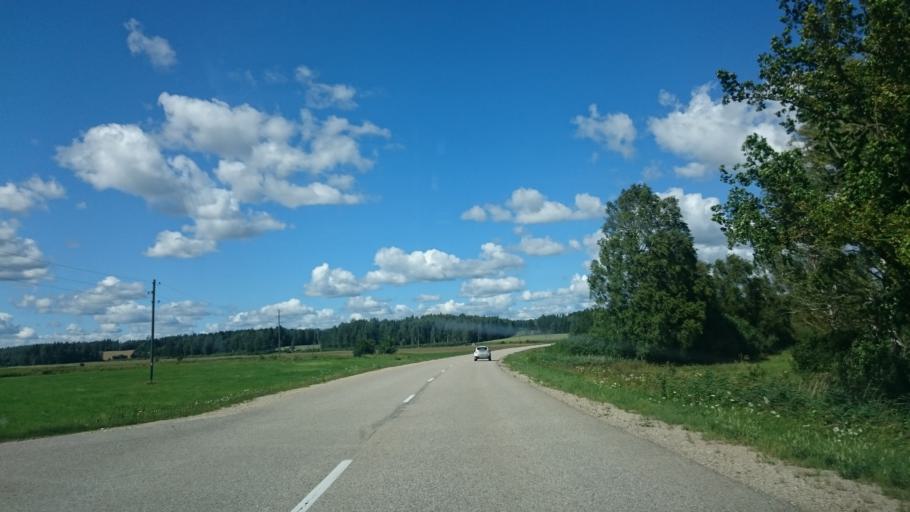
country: LV
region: Kuldigas Rajons
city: Kuldiga
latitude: 56.9166
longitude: 21.9052
